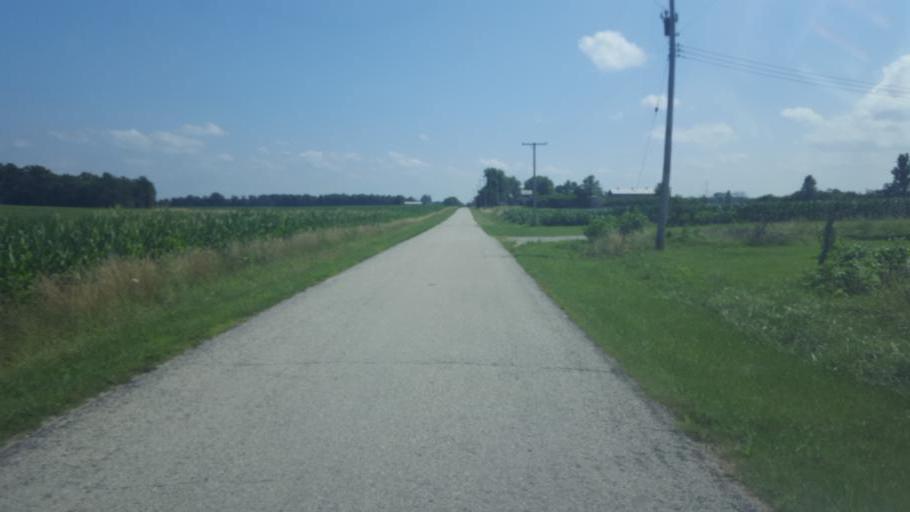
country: US
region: Ohio
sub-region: Huron County
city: Willard
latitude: 41.1391
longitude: -82.8150
